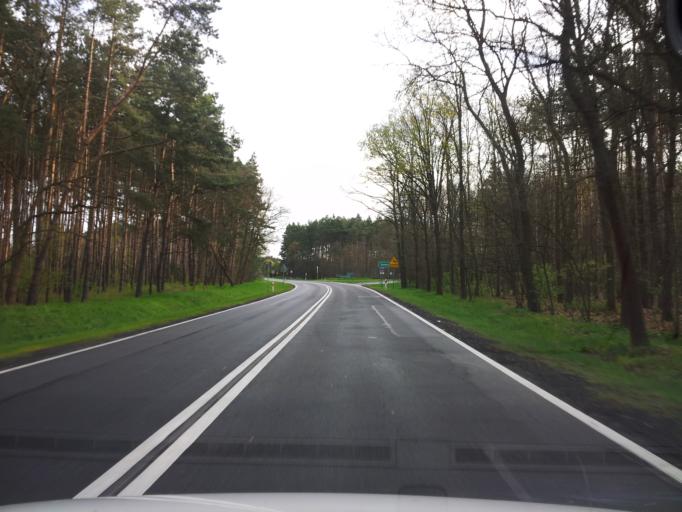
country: PL
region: Lubusz
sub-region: Powiat zielonogorski
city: Swidnica
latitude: 51.8806
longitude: 15.3783
